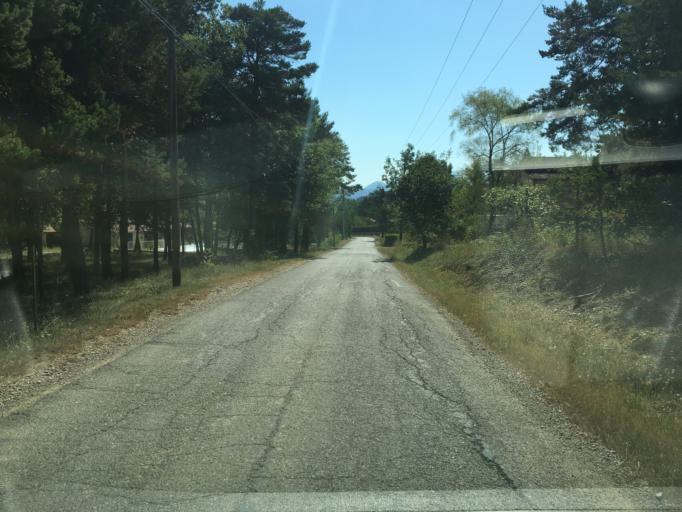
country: FR
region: Provence-Alpes-Cote d'Azur
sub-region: Departement des Alpes-de-Haute-Provence
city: Mallemoisson
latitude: 44.0676
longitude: 6.1384
